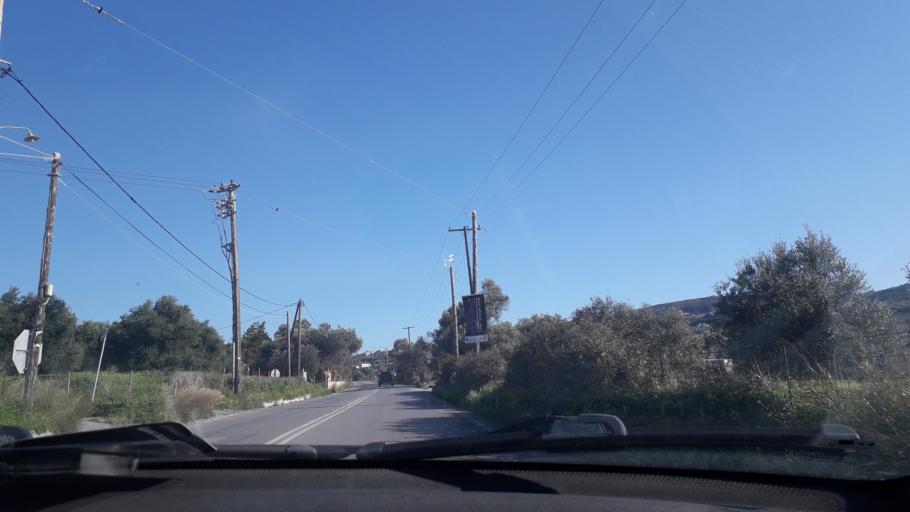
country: GR
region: Crete
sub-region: Nomos Rethymnis
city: Rethymno
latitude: 35.3649
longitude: 24.5401
